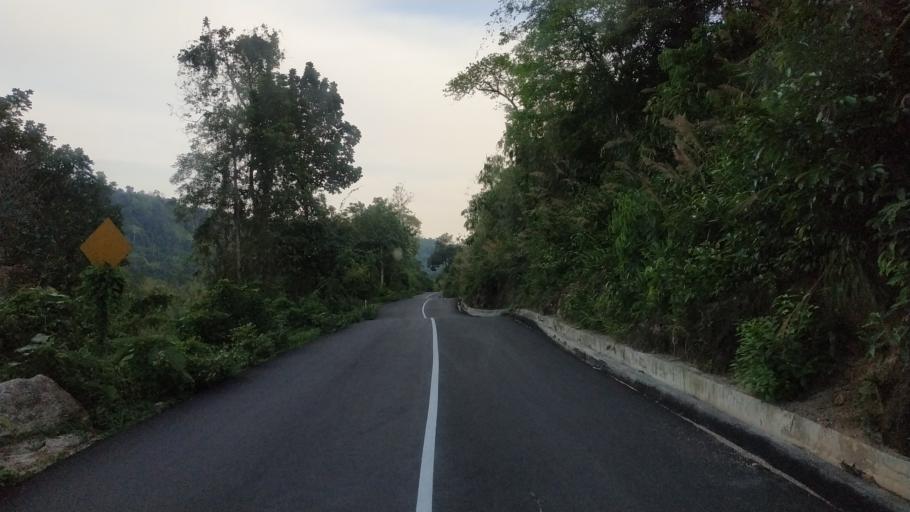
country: MM
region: Mon
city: Kyaikto
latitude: 17.4417
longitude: 97.0980
